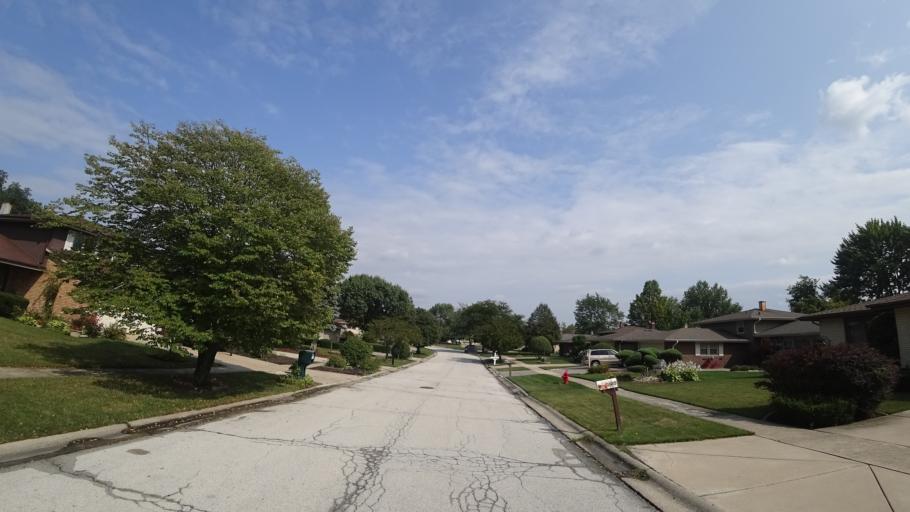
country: US
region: Illinois
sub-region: Cook County
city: Oak Forest
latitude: 41.6079
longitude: -87.7728
